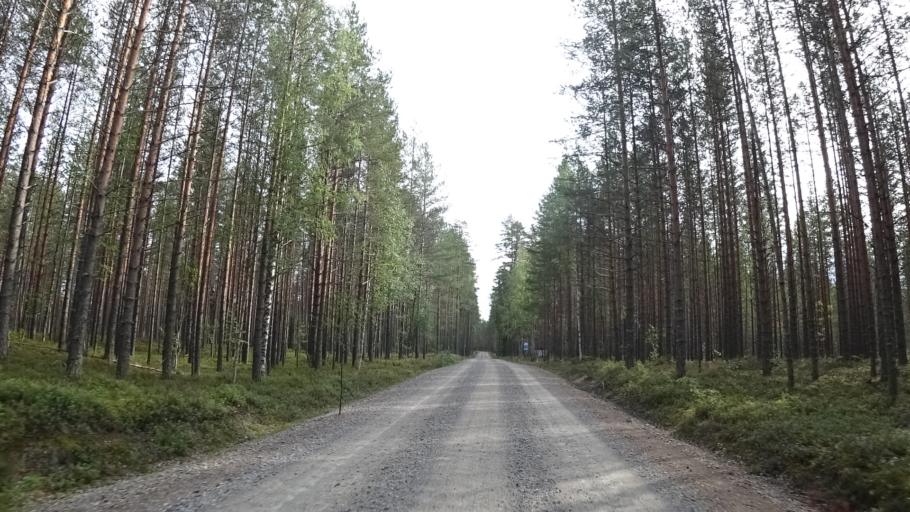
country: FI
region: North Karelia
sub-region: Joensuu
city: Ilomantsi
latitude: 62.6046
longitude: 31.1858
